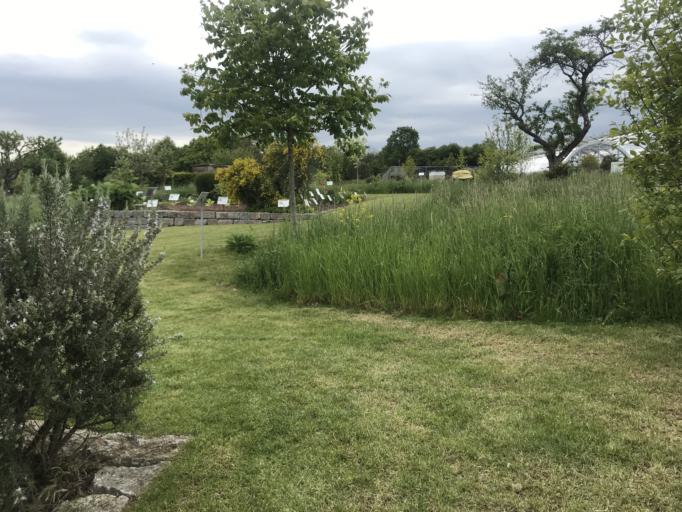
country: DE
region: Hesse
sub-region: Regierungsbezirk Darmstadt
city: Bad Homburg vor der Hoehe
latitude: 50.1703
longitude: 8.6308
